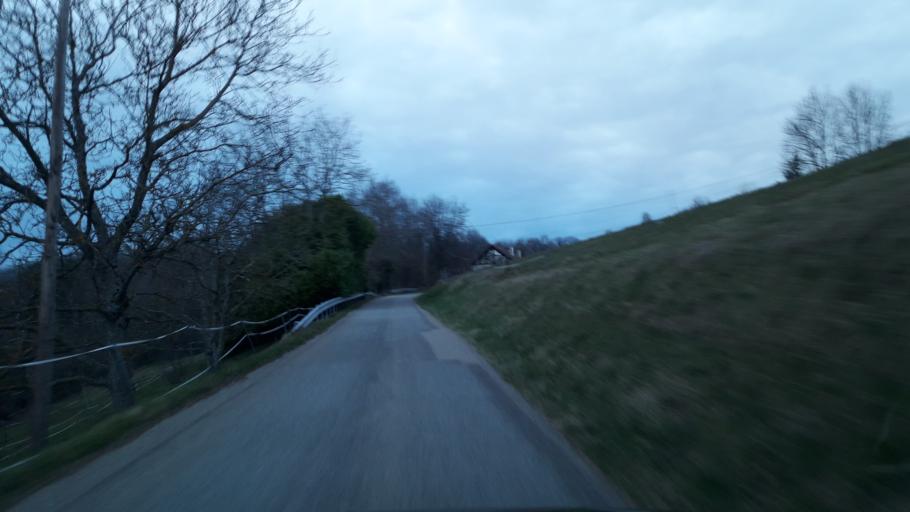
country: FR
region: Rhone-Alpes
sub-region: Departement de l'Isere
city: Herbeys
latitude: 45.1510
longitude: 5.7949
